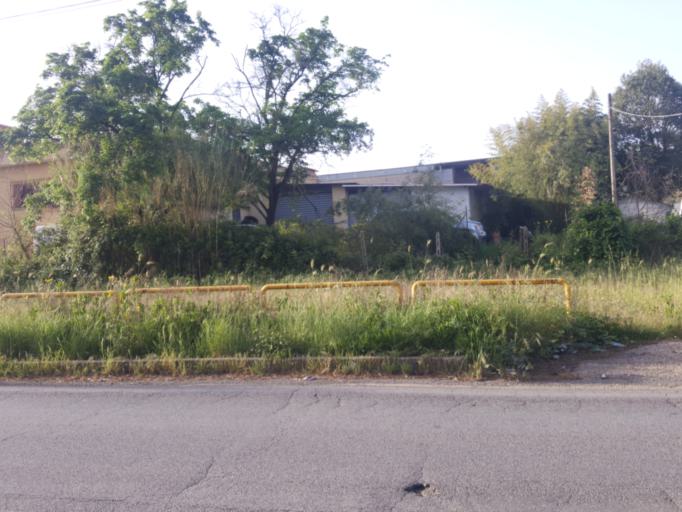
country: IT
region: Latium
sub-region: Citta metropolitana di Roma Capitale
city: Pavona
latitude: 41.7095
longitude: 12.6173
